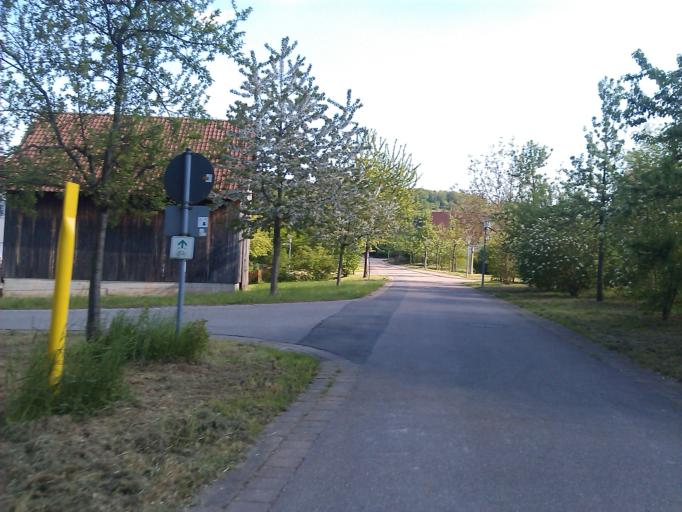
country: DE
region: Baden-Wuerttemberg
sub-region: Karlsruhe Region
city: Sternenfels
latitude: 49.0553
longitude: 8.8473
